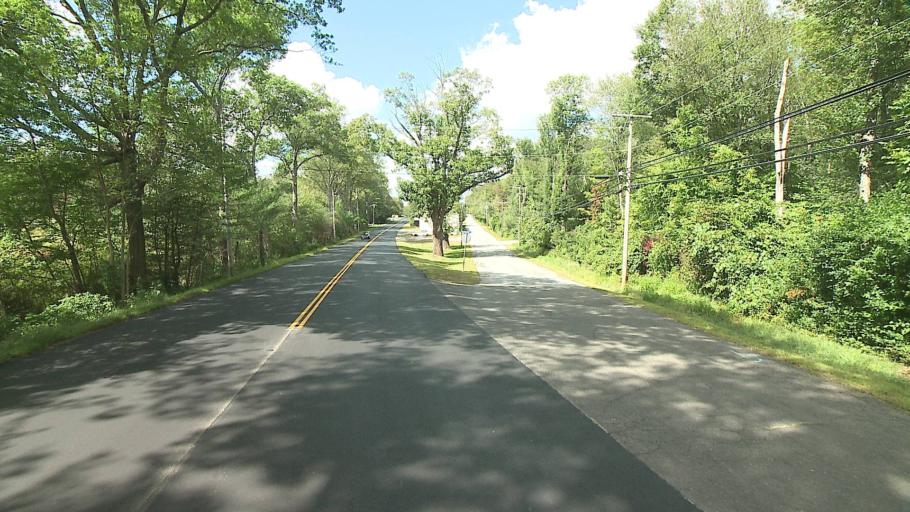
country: US
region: Connecticut
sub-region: Windham County
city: Thompson
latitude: 41.9263
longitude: -71.8617
